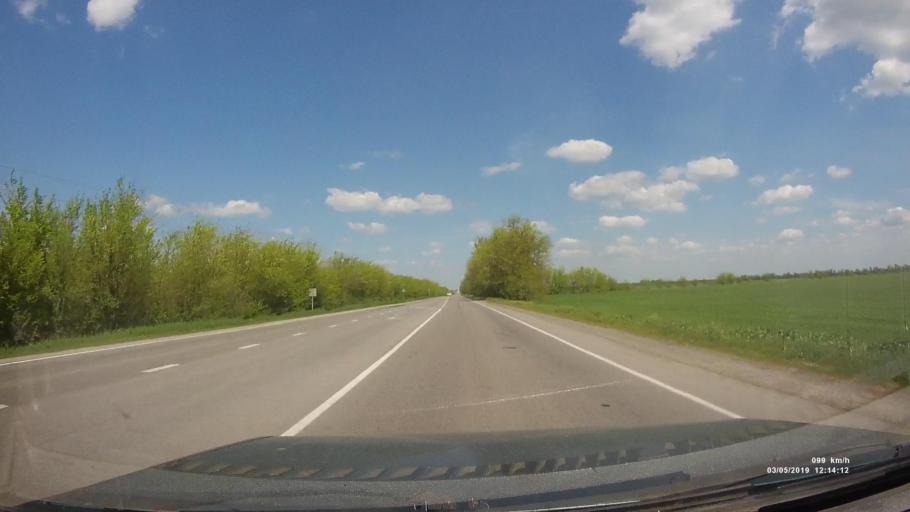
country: RU
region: Rostov
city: Melikhovskaya
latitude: 47.3407
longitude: 40.5610
